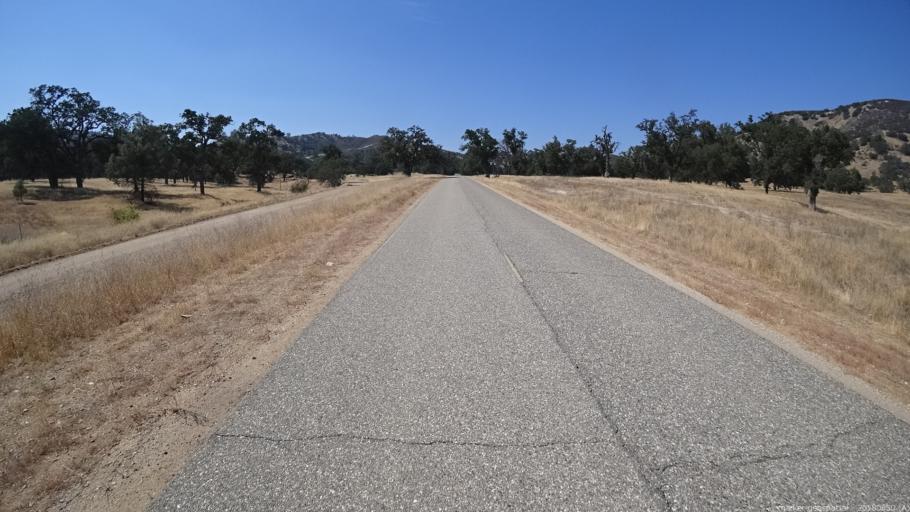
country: US
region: California
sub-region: Monterey County
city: King City
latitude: 36.0091
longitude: -121.2778
